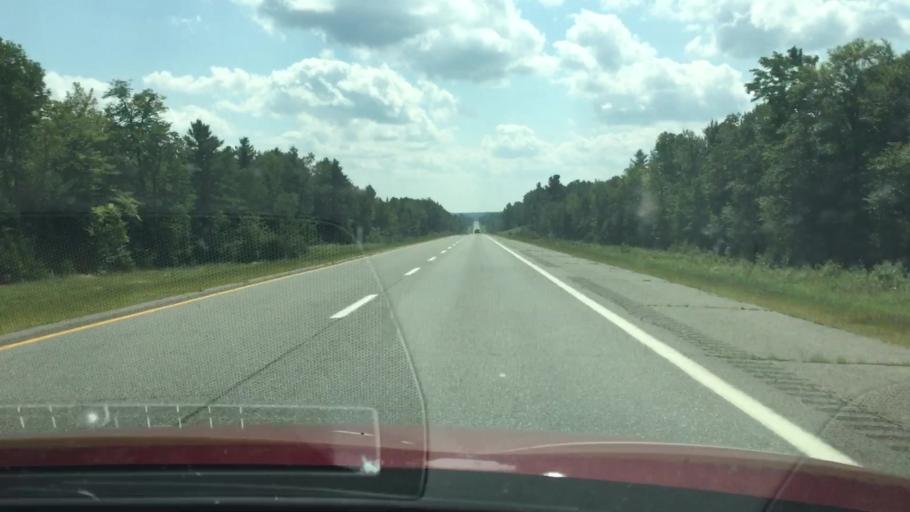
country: US
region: Maine
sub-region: Penobscot County
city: Lincoln
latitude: 45.4157
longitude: -68.5933
